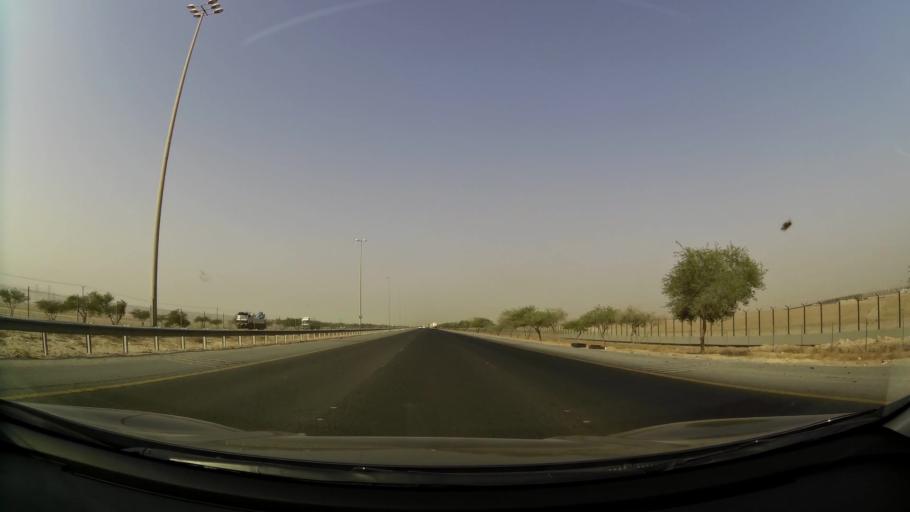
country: KW
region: Al Farwaniyah
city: Janub as Surrah
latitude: 29.1830
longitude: 47.9594
